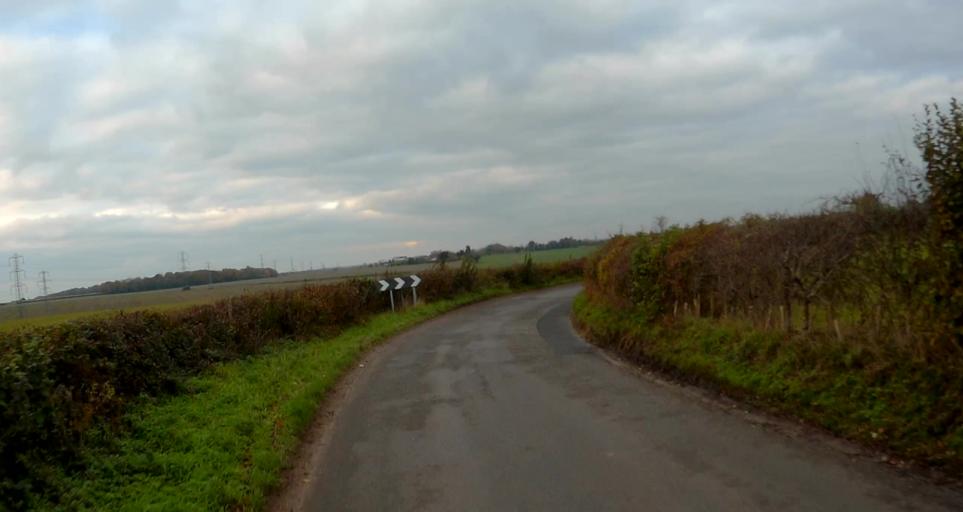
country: GB
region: England
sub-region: Hampshire
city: Long Sutton
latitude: 51.2251
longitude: -0.8800
